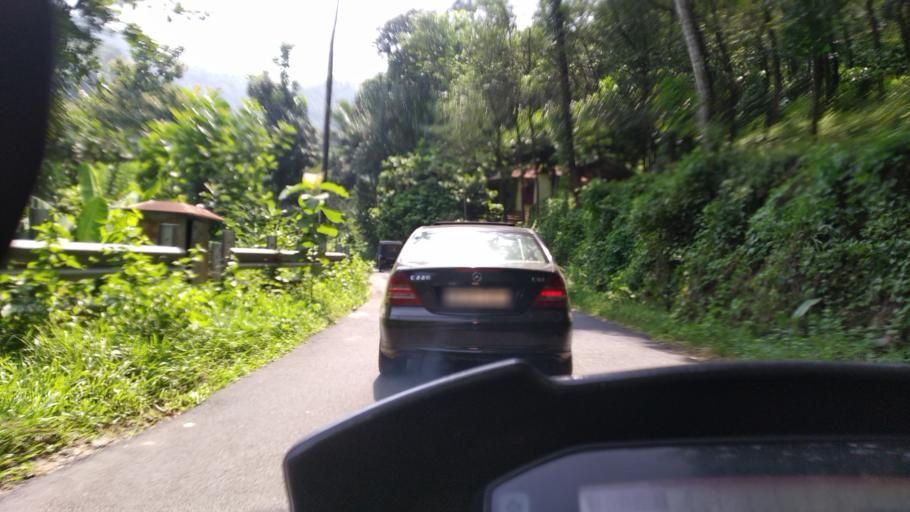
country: IN
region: Kerala
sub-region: Kottayam
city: Erattupetta
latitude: 9.6908
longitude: 76.8489
